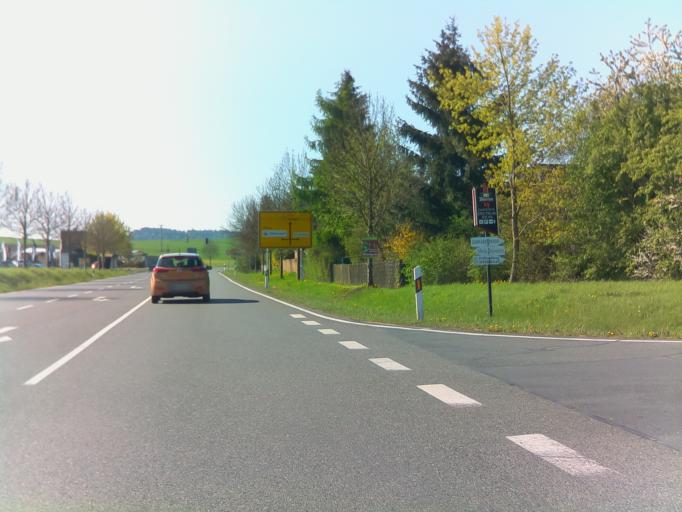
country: DE
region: Thuringia
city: Oettersdorf
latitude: 50.6037
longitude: 11.8239
